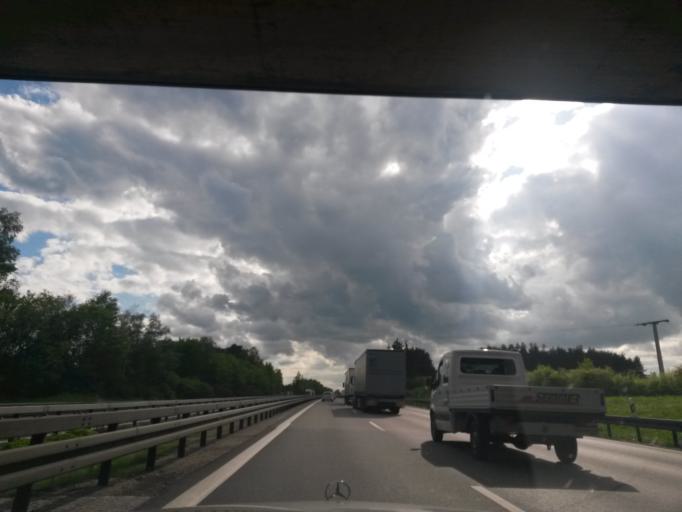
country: DE
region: Bavaria
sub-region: Regierungsbezirk Mittelfranken
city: Sachsen
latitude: 49.2680
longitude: 10.6997
